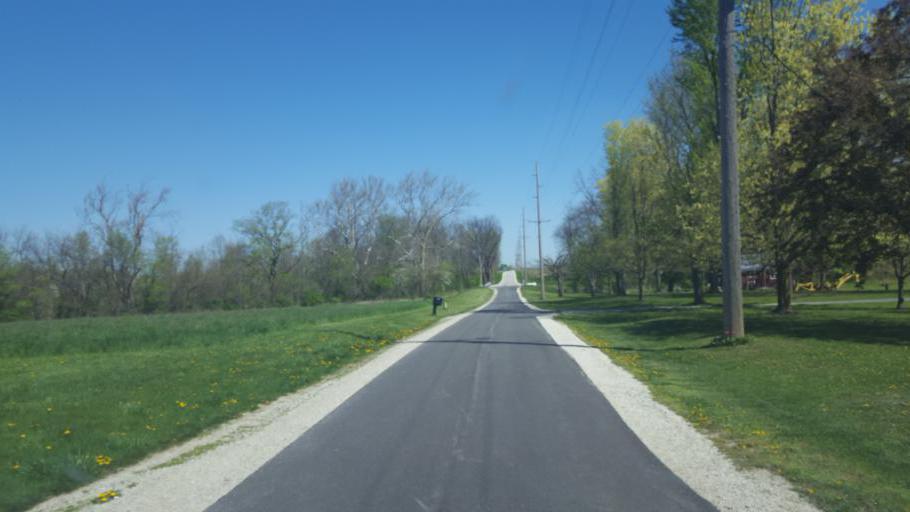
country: US
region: Ohio
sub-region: Sandusky County
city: Ballville
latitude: 41.2686
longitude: -83.1879
